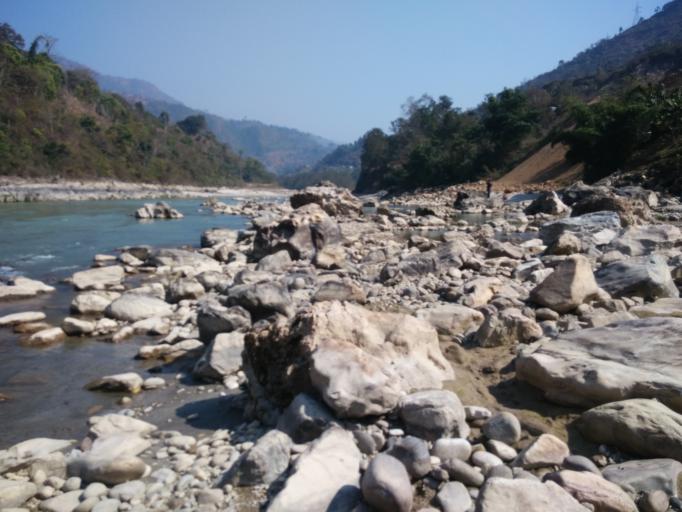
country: NP
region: Central Region
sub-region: Narayani Zone
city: Bharatpur
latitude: 27.8141
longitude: 84.7966
